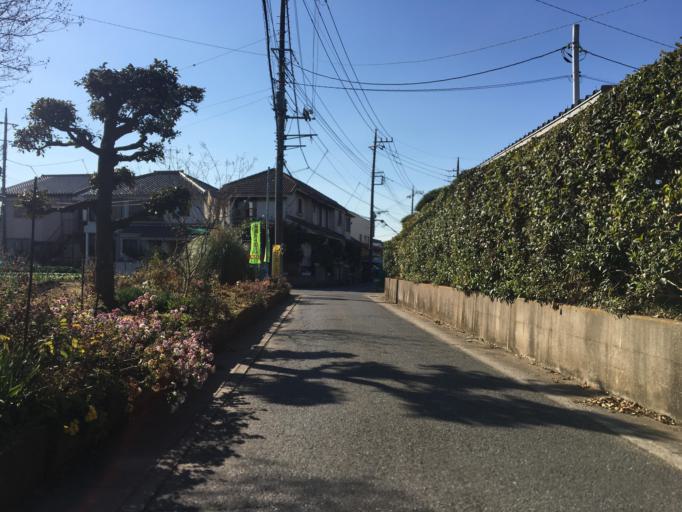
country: JP
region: Saitama
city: Yashio-shi
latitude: 35.8056
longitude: 139.8540
